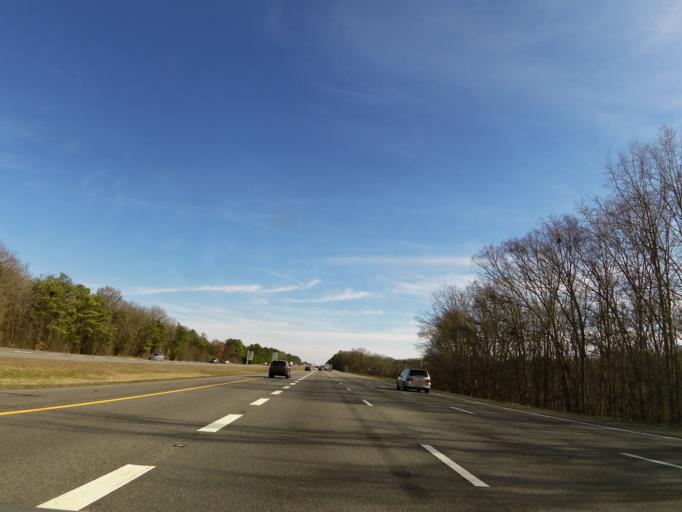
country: US
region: Tennessee
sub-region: Rutherford County
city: Smyrna
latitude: 35.9108
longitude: -86.5056
